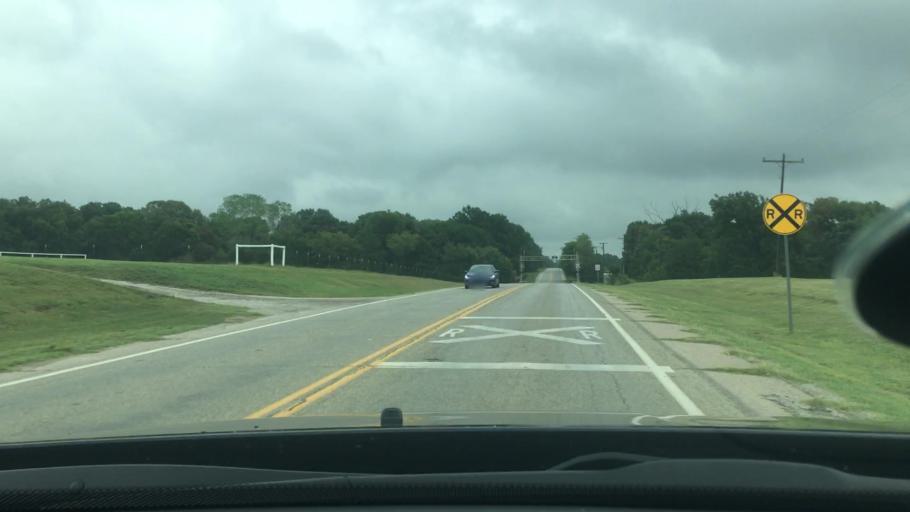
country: US
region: Oklahoma
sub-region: Bryan County
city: Colbert
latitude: 33.8529
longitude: -96.5310
